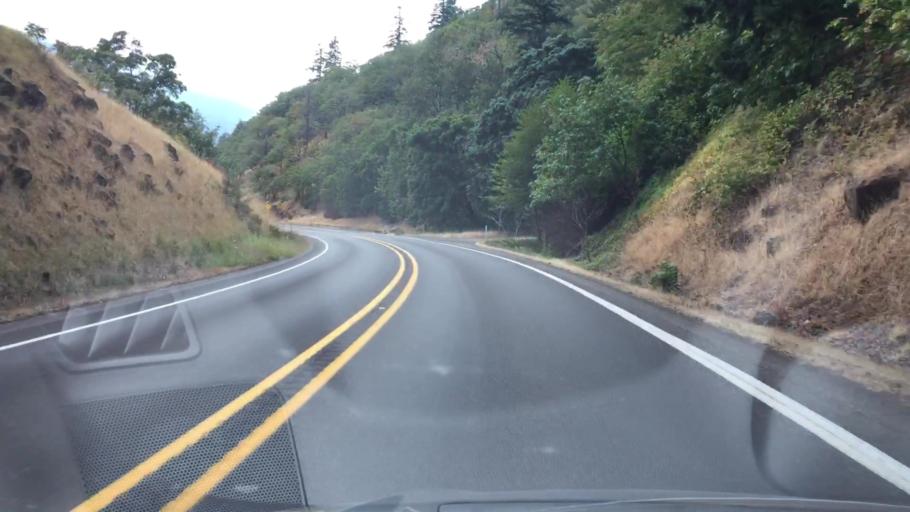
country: US
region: Oregon
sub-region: Hood River County
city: Hood River
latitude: 45.7209
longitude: -121.6045
